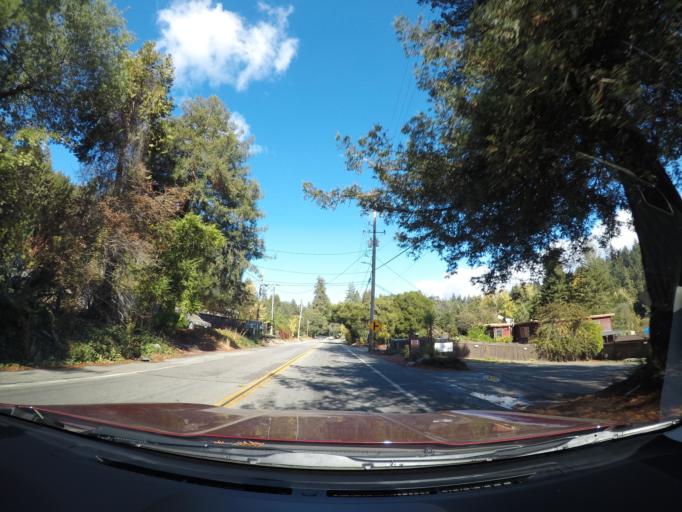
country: US
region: California
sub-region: Santa Cruz County
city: Ben Lomond
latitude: 37.0942
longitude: -122.0968
